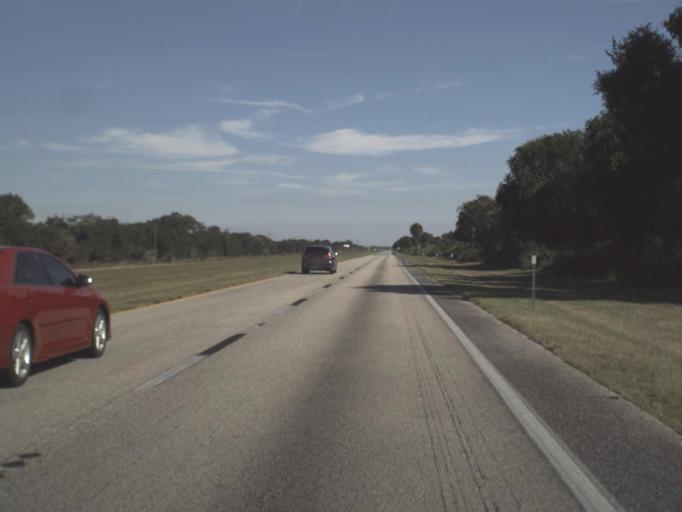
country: US
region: Florida
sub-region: Hendry County
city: Port LaBelle
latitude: 26.9217
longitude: -81.3037
